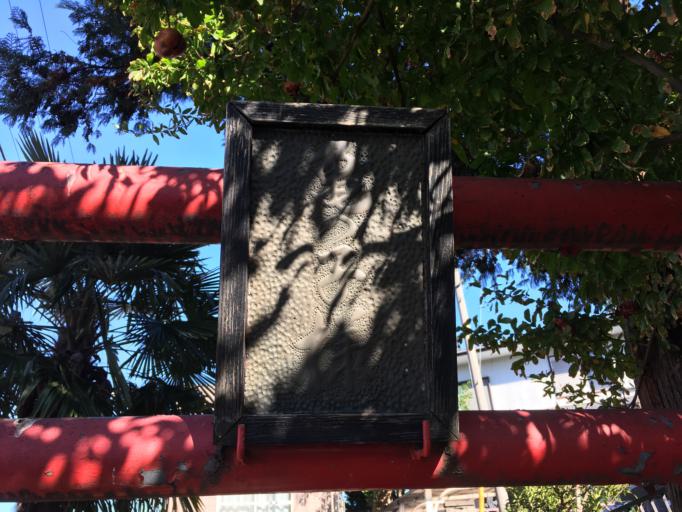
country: JP
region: Kanagawa
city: Yokohama
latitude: 35.4191
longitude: 139.6632
